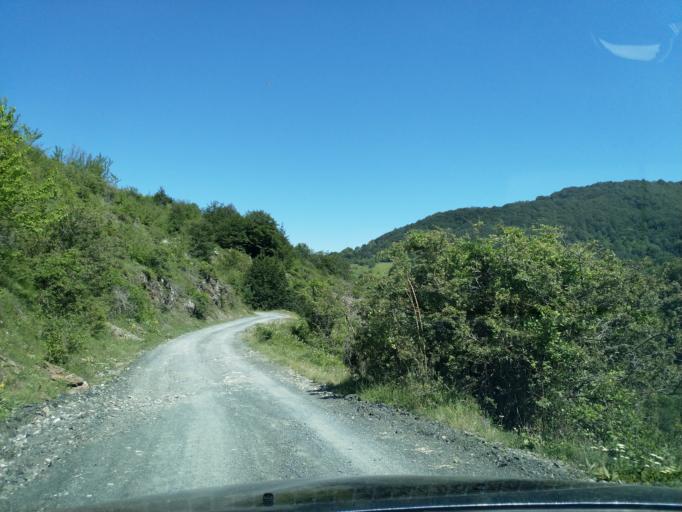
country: XK
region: Mitrovica
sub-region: Komuna e Leposaviqit
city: Leposaviq
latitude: 43.2647
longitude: 20.8626
